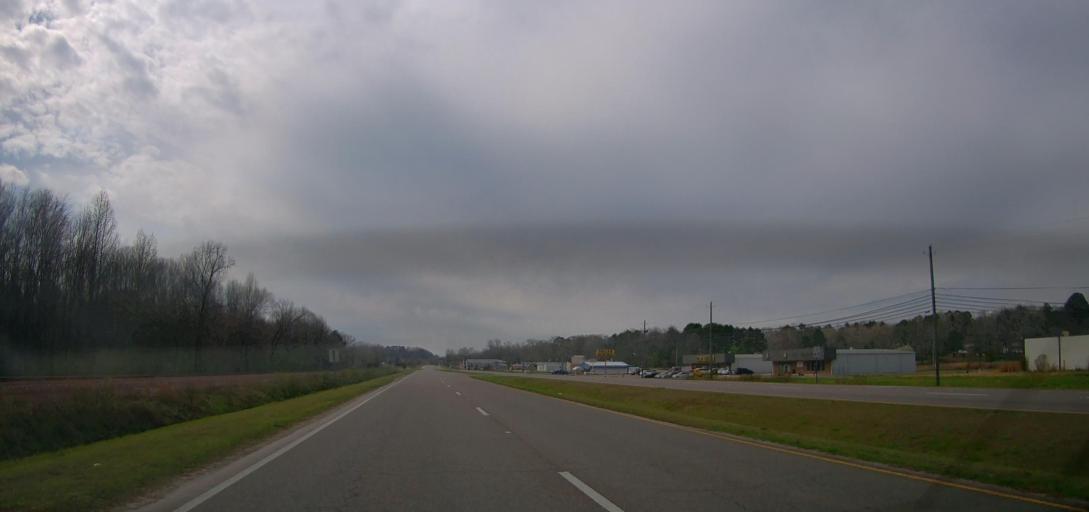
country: US
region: Alabama
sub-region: Walker County
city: Carbon Hill
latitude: 33.8848
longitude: -87.5187
